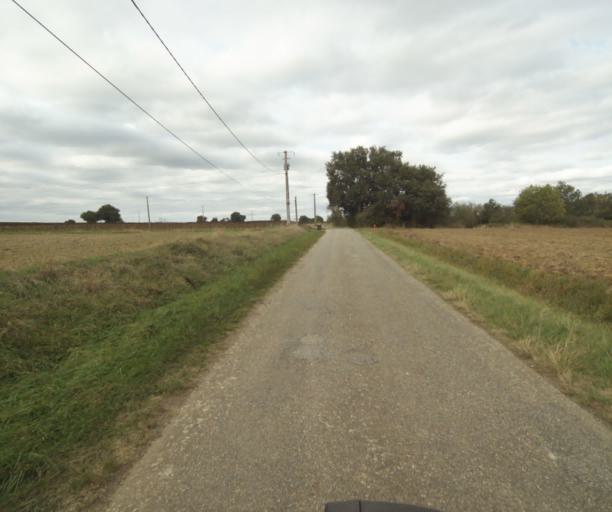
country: FR
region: Midi-Pyrenees
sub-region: Departement du Tarn-et-Garonne
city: Verdun-sur-Garonne
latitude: 43.8685
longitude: 1.1697
